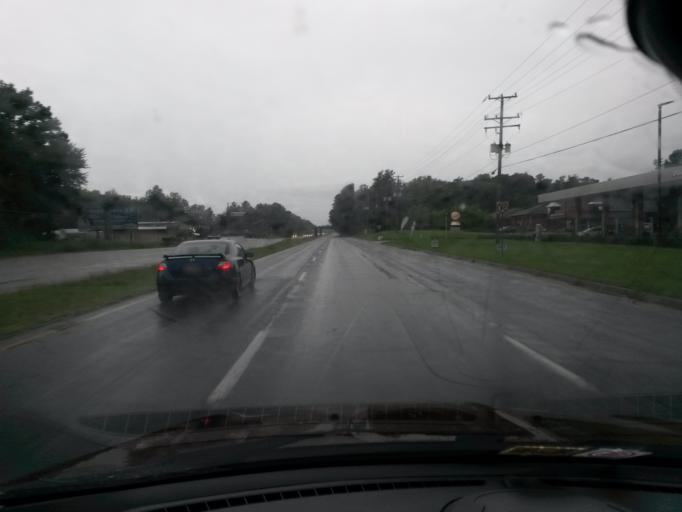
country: US
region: Virginia
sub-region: Chesterfield County
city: Enon
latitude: 37.3344
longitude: -77.3264
